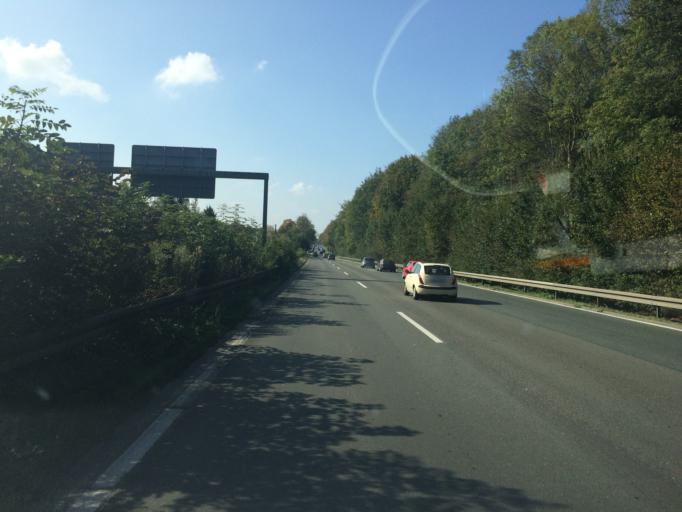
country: DE
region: North Rhine-Westphalia
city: Schwerte
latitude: 51.5094
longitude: 7.5475
